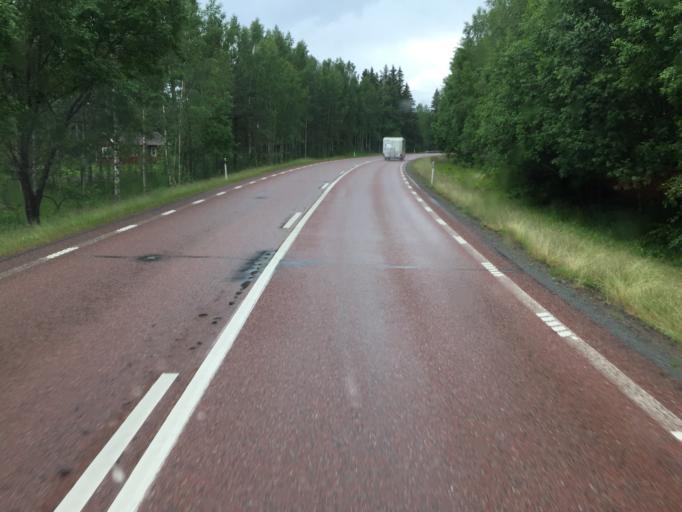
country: SE
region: Dalarna
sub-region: Malung-Saelens kommun
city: Malung
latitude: 60.6227
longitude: 13.7736
